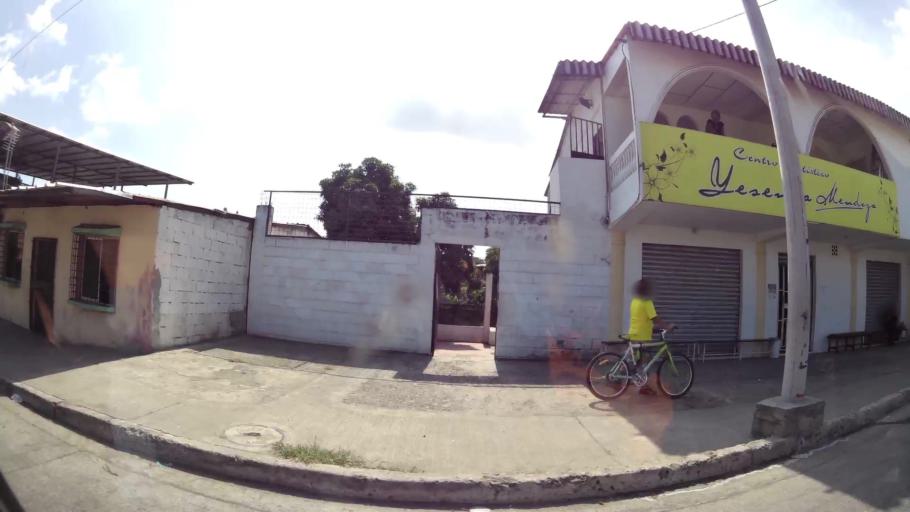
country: EC
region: Guayas
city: Santa Lucia
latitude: -2.1417
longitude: -79.9420
